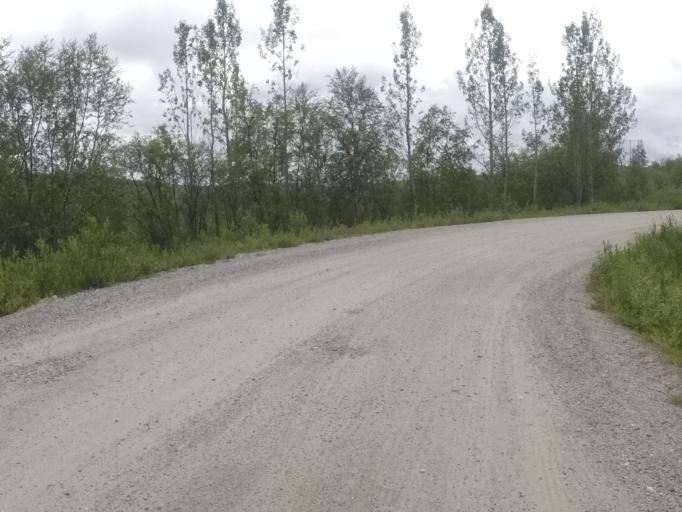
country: NO
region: Finnmark Fylke
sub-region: Alta
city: Alta
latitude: 69.4256
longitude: 23.6202
